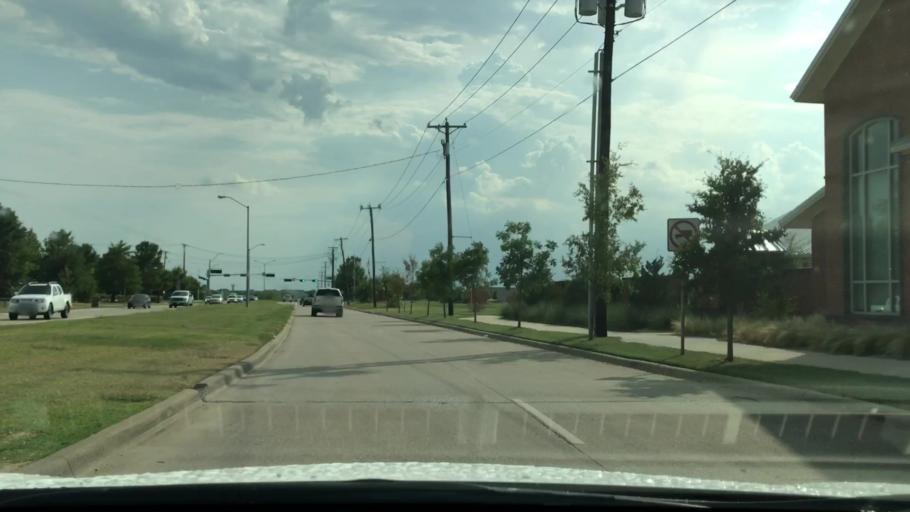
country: US
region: Texas
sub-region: Dallas County
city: Rowlett
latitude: 32.9361
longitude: -96.5367
